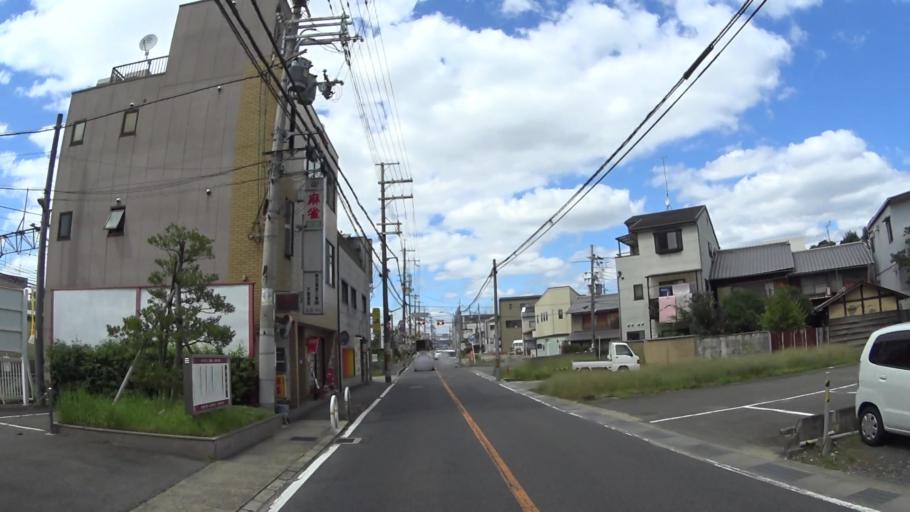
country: JP
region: Kyoto
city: Uji
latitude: 34.9138
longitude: 135.8035
